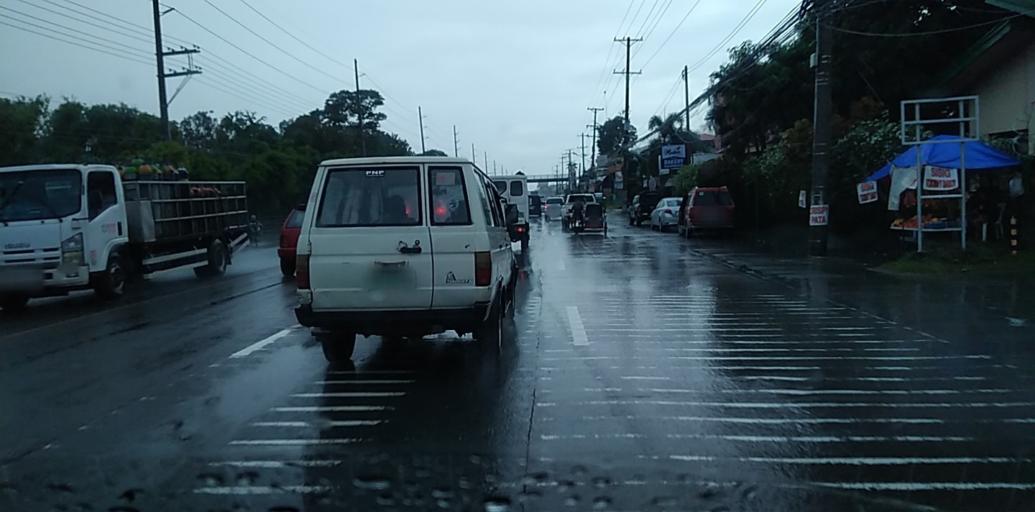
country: PH
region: Central Luzon
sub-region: Province of Pampanga
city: Magliman
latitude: 15.0580
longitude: 120.6578
